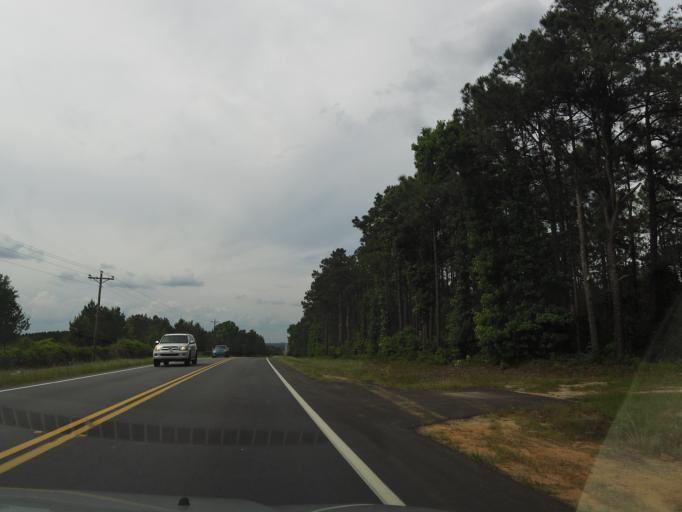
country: US
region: Georgia
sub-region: Jefferson County
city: Wrens
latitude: 33.3231
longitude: -82.4521
